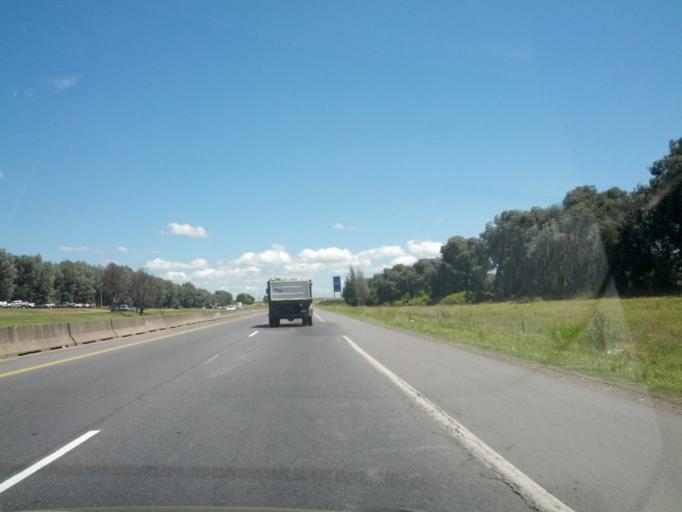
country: AR
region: Buenos Aires
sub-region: Partido de Zarate
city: Zarate
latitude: -34.1330
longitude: -59.0410
